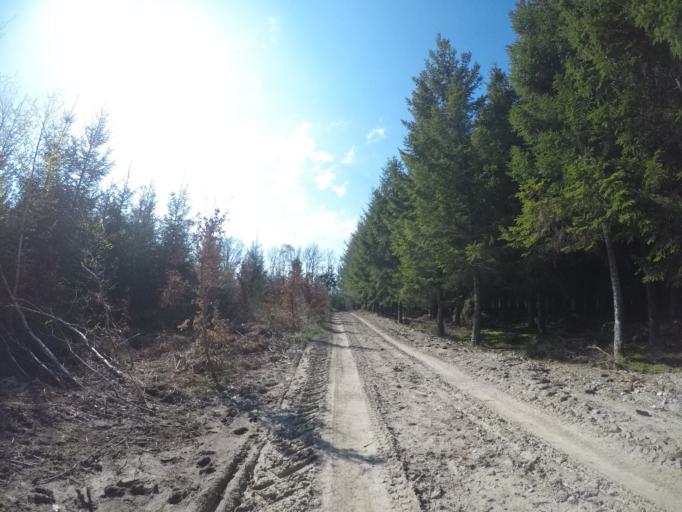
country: BE
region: Wallonia
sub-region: Province du Luxembourg
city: Leglise
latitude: 49.7878
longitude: 5.5825
